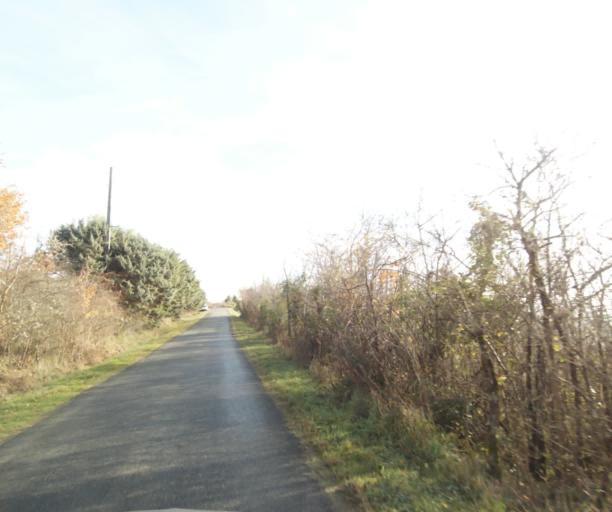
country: FR
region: Midi-Pyrenees
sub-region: Departement de la Haute-Garonne
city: Villemur-sur-Tarn
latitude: 43.8565
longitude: 1.5153
